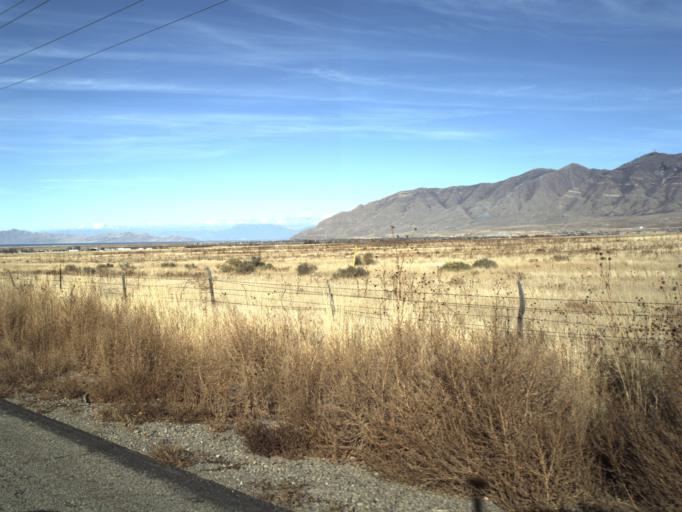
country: US
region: Utah
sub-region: Tooele County
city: Erda
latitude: 40.5731
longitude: -112.3673
